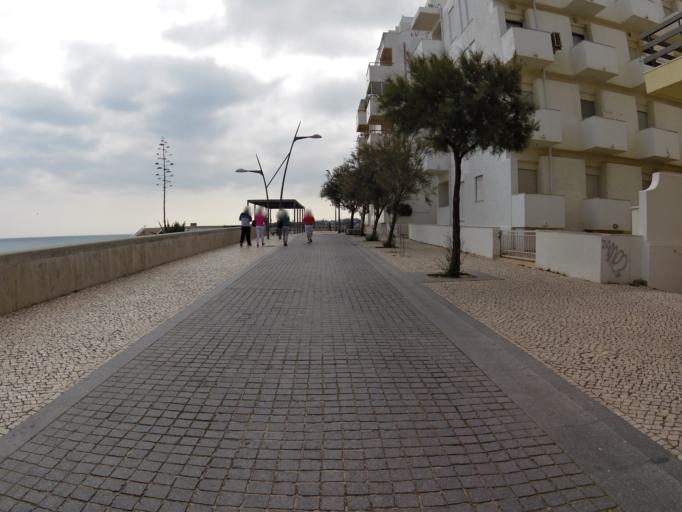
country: PT
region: Faro
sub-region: Silves
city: Armacao de Pera
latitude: 37.1012
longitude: -8.3614
